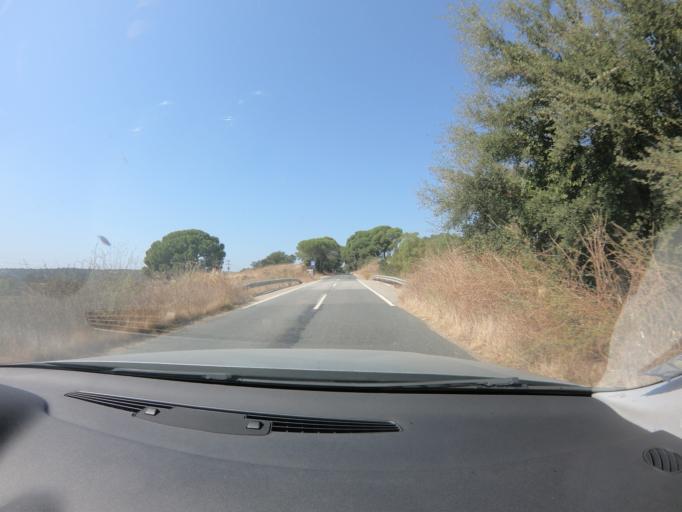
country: PT
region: Setubal
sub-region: Alcacer do Sal
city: Alcacer do Sal
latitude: 38.2737
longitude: -8.3712
